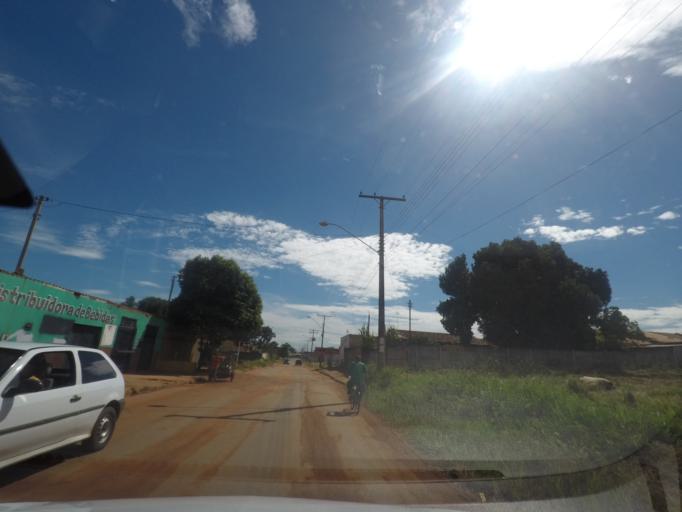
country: BR
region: Goias
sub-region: Aparecida De Goiania
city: Aparecida de Goiania
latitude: -16.8051
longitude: -49.2864
